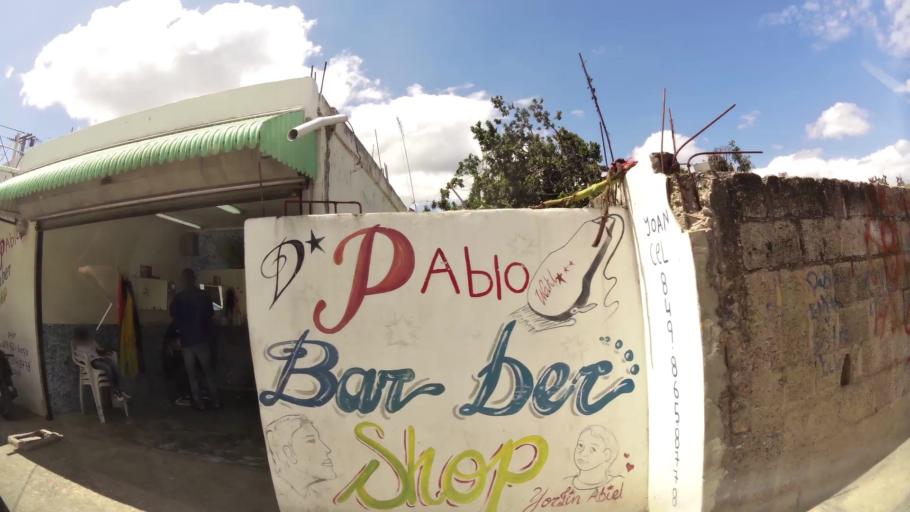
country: DO
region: San Cristobal
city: San Cristobal
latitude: 18.4085
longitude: -70.1026
